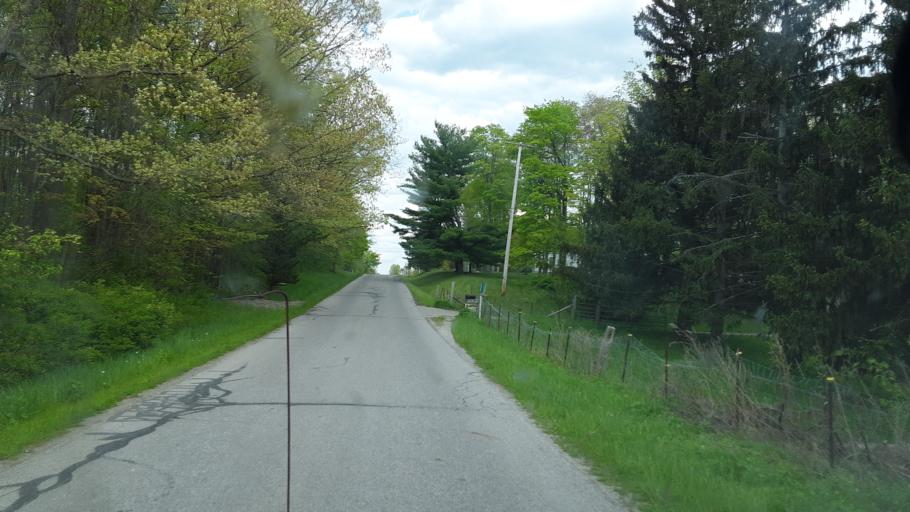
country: US
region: Ohio
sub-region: Portage County
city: Garrettsville
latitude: 41.3479
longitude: -81.0108
